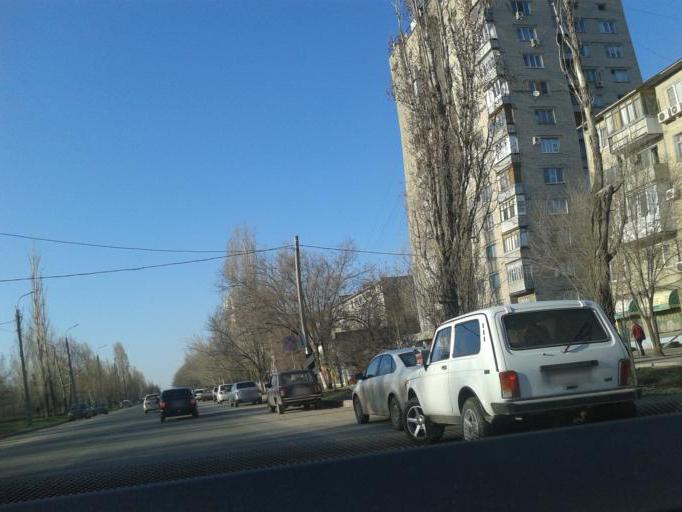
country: RU
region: Volgograd
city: Gorodishche
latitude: 48.7626
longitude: 44.4784
